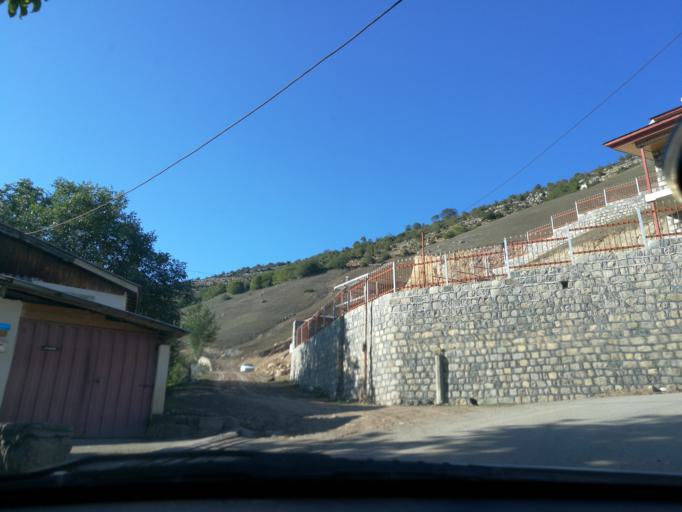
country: IR
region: Mazandaran
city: `Abbasabad
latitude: 36.5589
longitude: 51.1885
